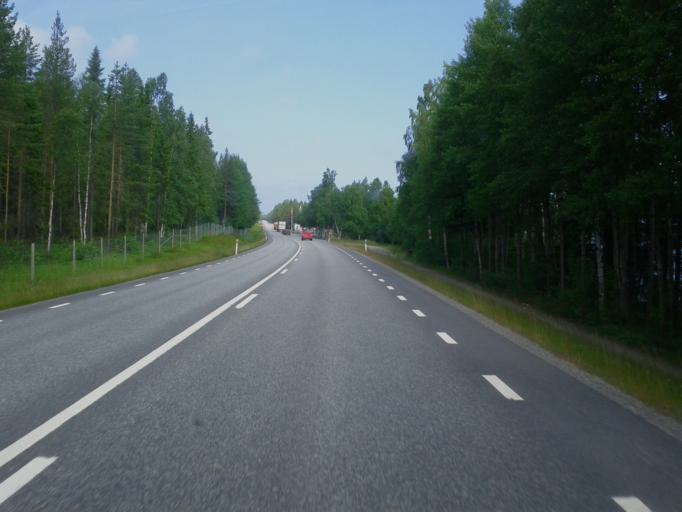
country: SE
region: Vaesterbotten
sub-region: Skelleftea Kommun
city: Burea
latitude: 64.5363
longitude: 21.2584
